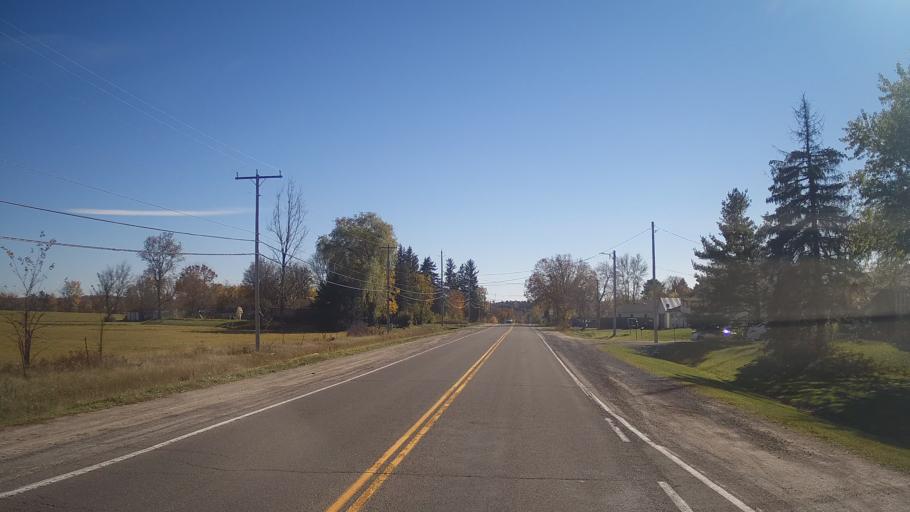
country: CA
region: Ontario
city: Kingston
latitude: 44.4103
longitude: -76.6661
